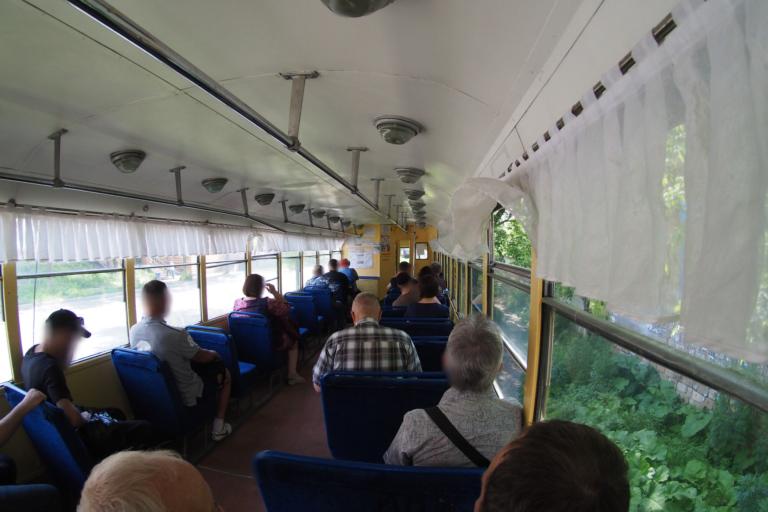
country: RU
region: Primorskiy
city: Vladivostok
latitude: 43.0976
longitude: 131.9658
